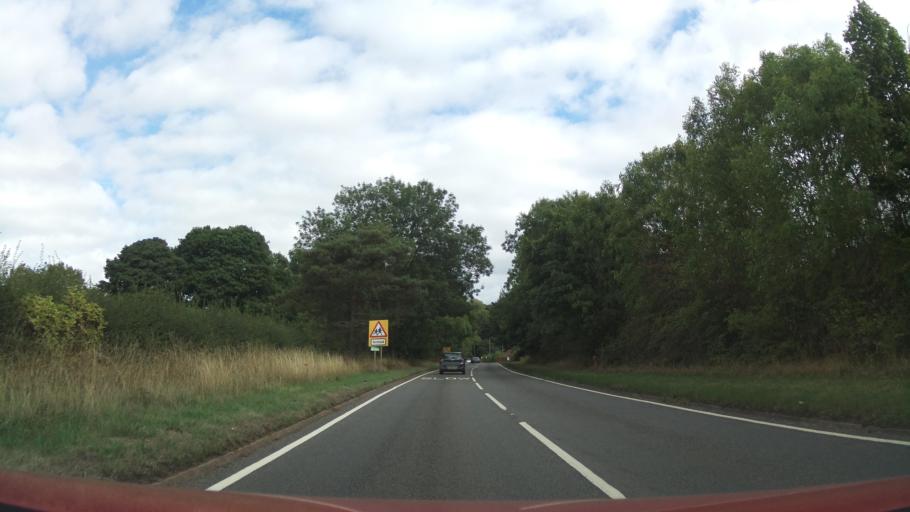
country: GB
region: England
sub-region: Leicestershire
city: Coalville
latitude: 52.7608
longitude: -1.3514
